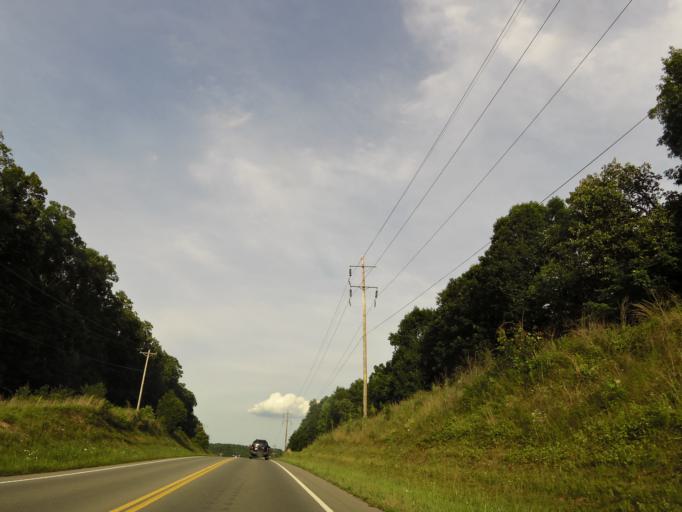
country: US
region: Tennessee
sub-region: Humphreys County
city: McEwen
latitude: 36.0978
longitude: -87.5993
